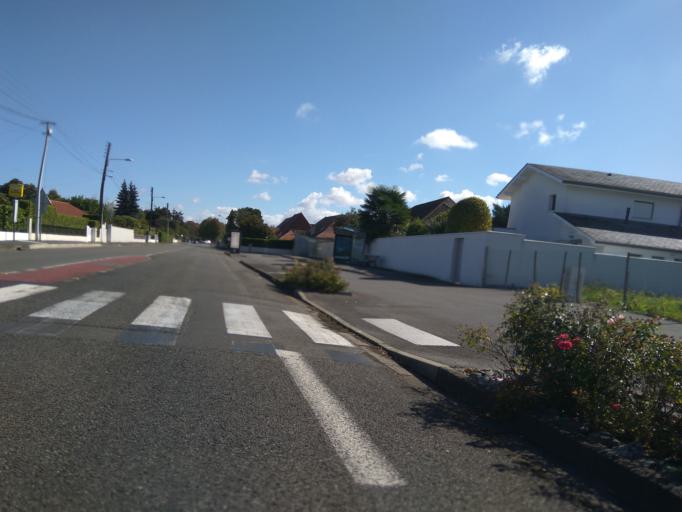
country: FR
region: Aquitaine
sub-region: Departement des Pyrenees-Atlantiques
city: Idron
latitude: 43.2990
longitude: -0.3212
